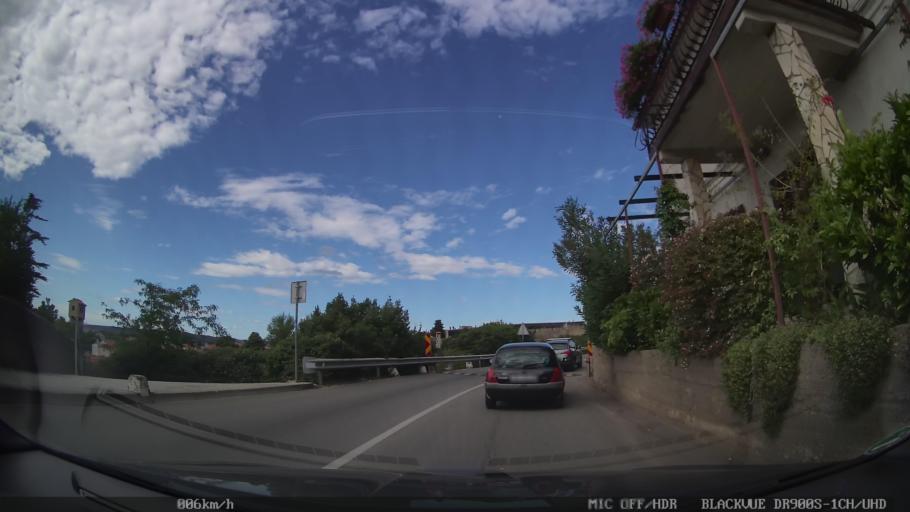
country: HR
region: Primorsko-Goranska
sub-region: Grad Krk
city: Krk
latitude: 45.0286
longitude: 14.5787
